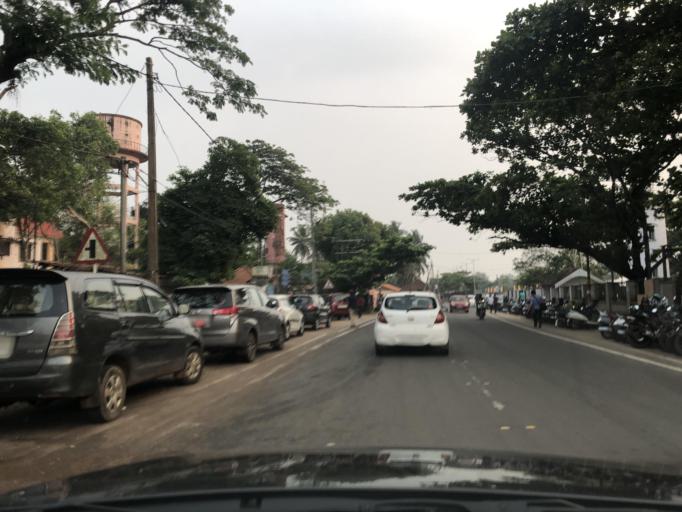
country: IN
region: Kerala
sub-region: Kozhikode
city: Kozhikode
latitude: 11.2591
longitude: 75.7692
